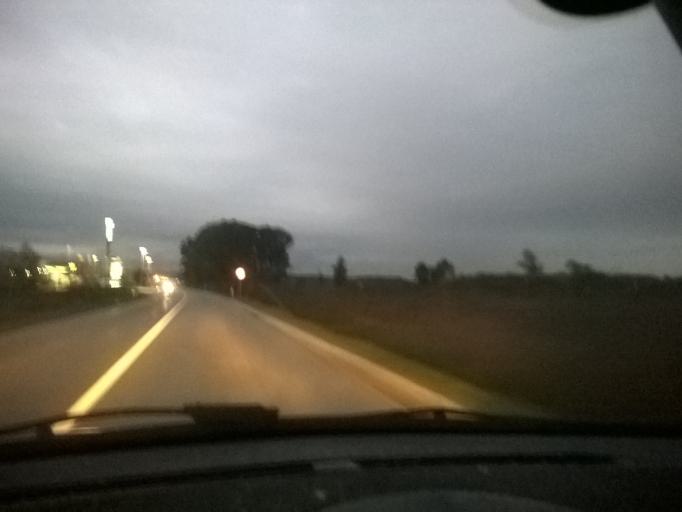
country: HR
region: Krapinsko-Zagorska
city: Zabok
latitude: 46.0146
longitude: 15.8876
